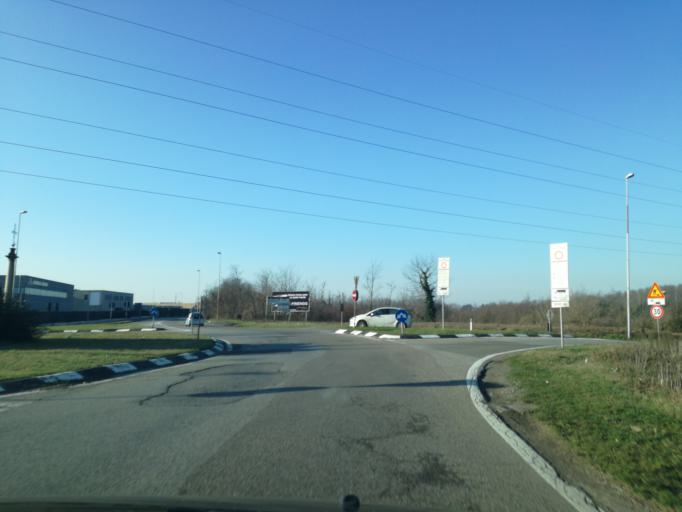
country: IT
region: Lombardy
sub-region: Provincia di Monza e Brianza
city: Villanova
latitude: 45.6369
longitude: 9.3973
